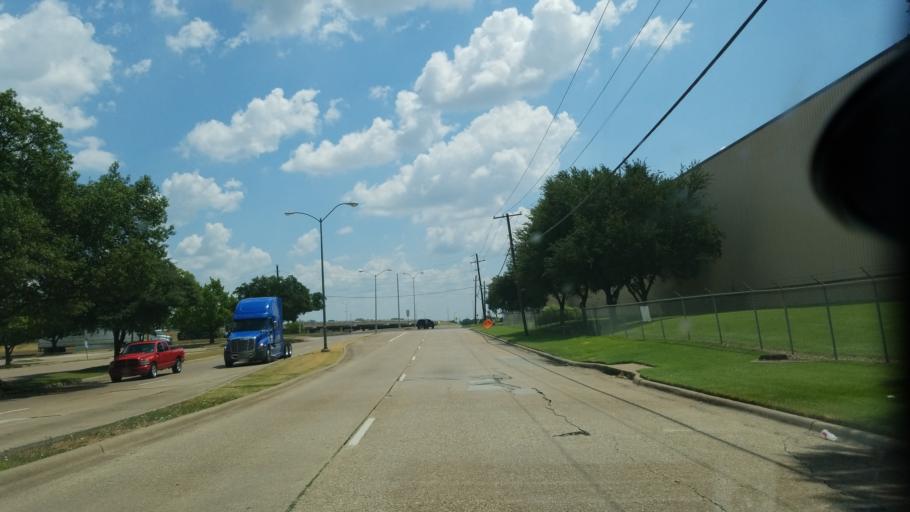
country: US
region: Texas
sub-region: Dallas County
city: Duncanville
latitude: 32.6911
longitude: -96.8947
